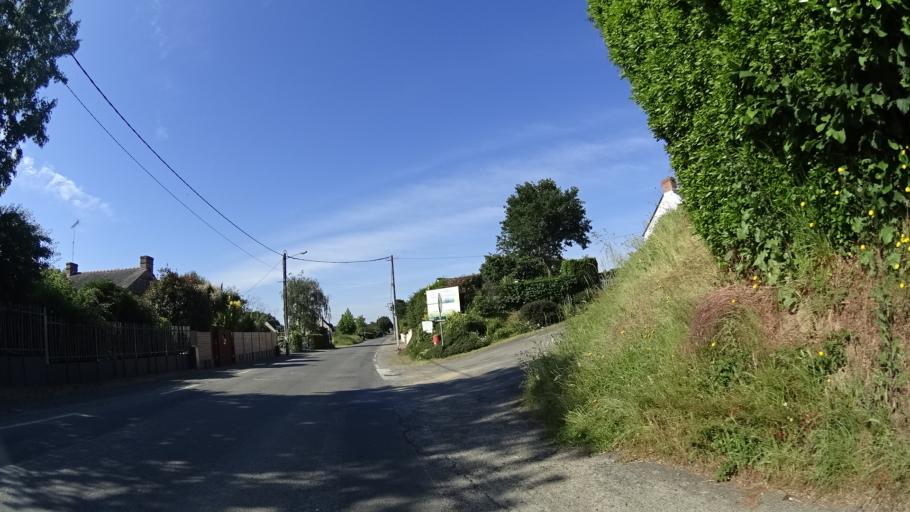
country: FR
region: Brittany
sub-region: Departement d'Ille-et-Vilaine
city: Guipry
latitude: 47.8218
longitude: -1.8446
